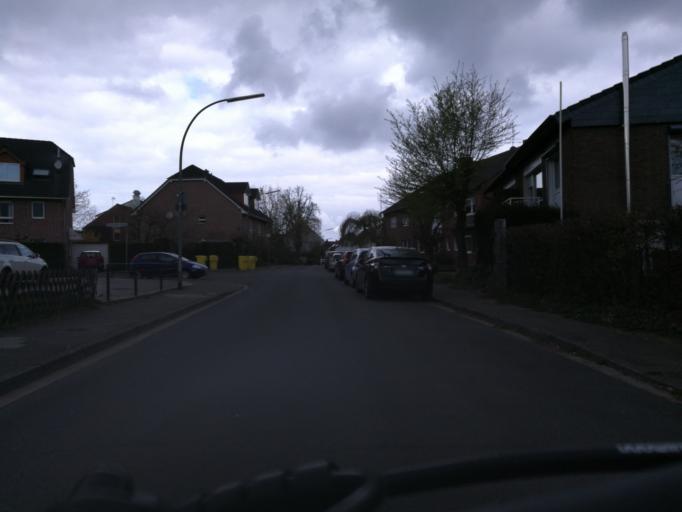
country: DE
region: North Rhine-Westphalia
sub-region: Regierungsbezirk Dusseldorf
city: Dusseldorf
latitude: 51.1607
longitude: 6.7904
